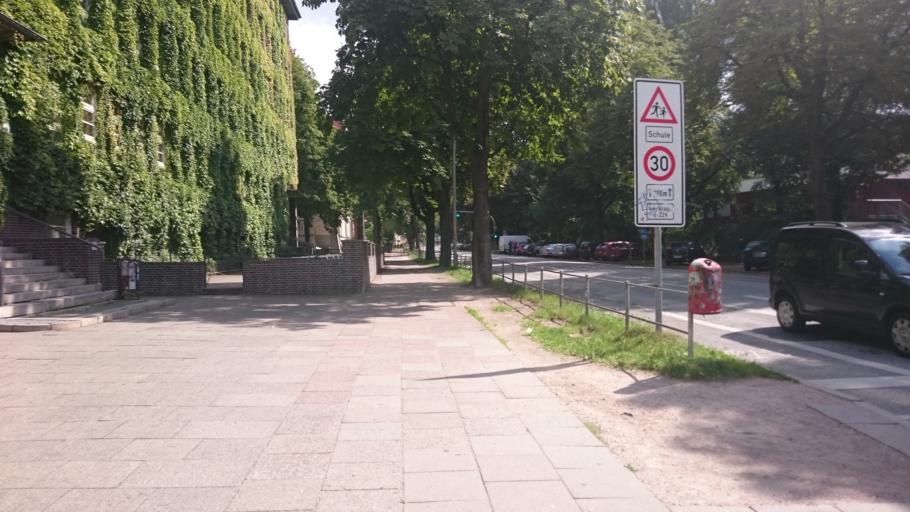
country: DE
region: Hamburg
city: Eimsbuettel
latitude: 53.5743
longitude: 9.9734
